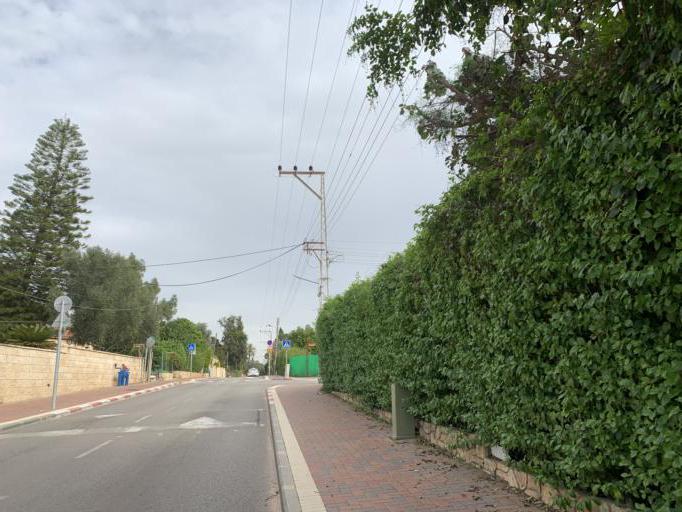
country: IL
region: Central District
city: Hod HaSharon
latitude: 32.1515
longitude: 34.8987
